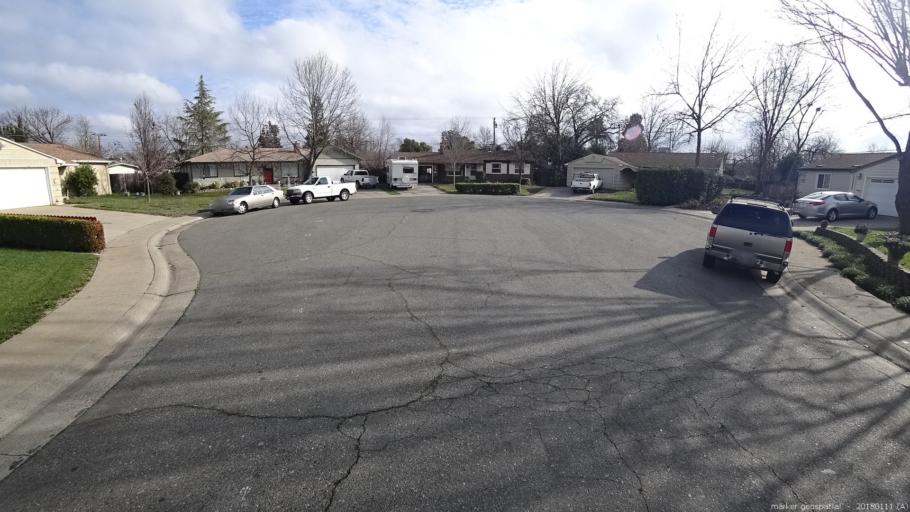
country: US
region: California
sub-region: Sacramento County
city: Rancho Cordova
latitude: 38.6100
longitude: -121.2956
